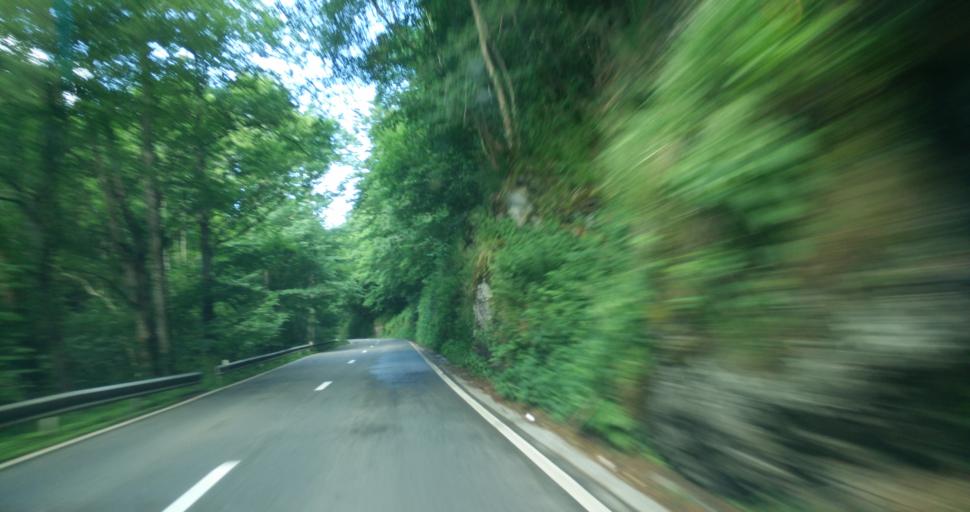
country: BE
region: Wallonia
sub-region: Province du Luxembourg
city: La Roche-en-Ardenne
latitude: 50.1762
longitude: 5.6373
